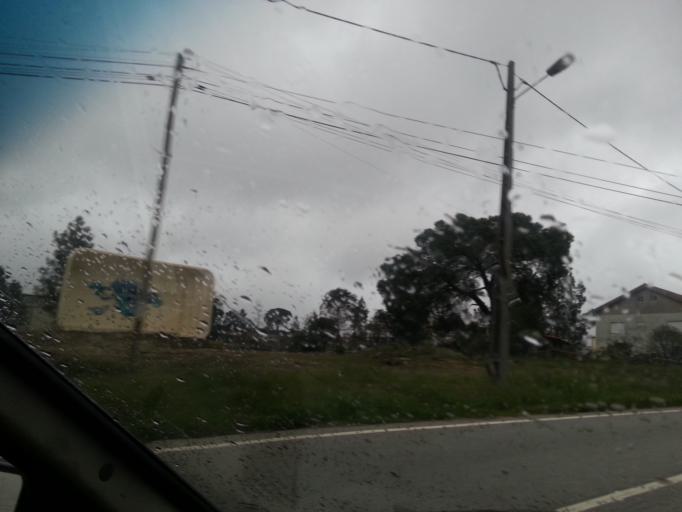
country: PT
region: Viseu
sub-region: Mangualde
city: Mangualde
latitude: 40.6017
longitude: -7.7896
